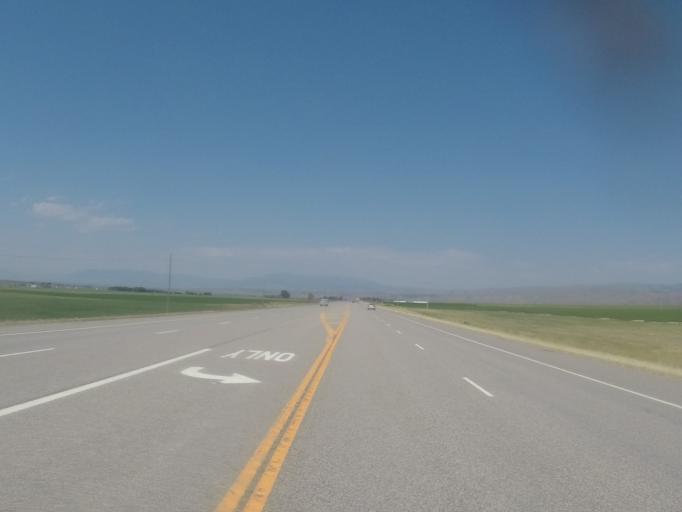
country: US
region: Montana
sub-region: Broadwater County
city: Townsend
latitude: 46.1231
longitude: -111.4951
